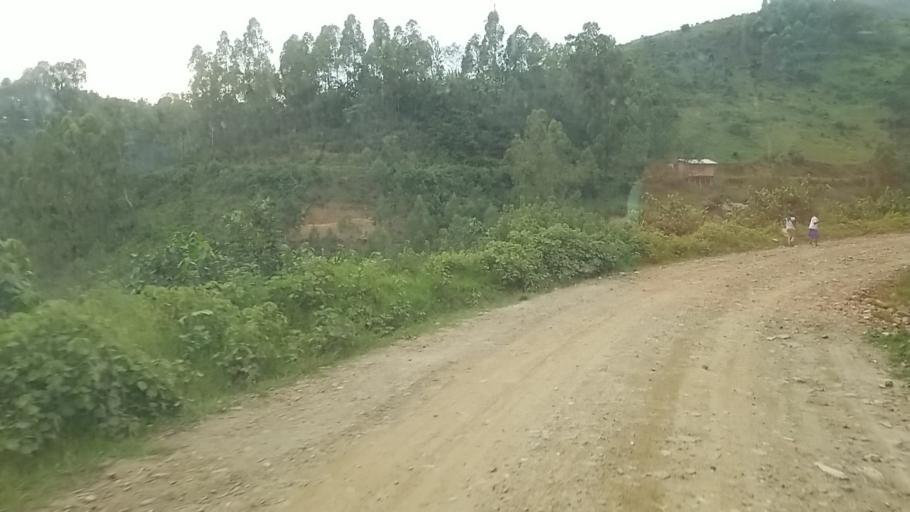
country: CD
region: Nord Kivu
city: Sake
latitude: -1.9554
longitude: 28.9225
